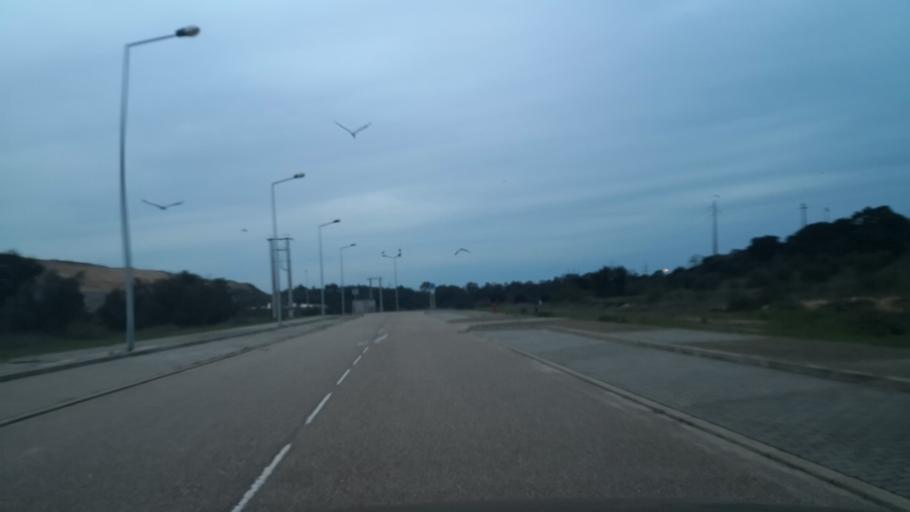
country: PT
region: Setubal
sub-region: Setubal
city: Setubal
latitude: 38.4972
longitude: -8.8143
